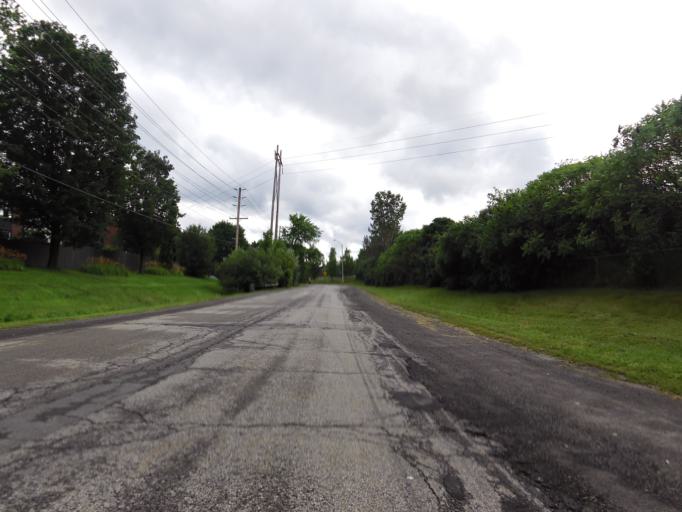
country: CA
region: Ontario
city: Bells Corners
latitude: 45.3198
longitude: -75.7845
